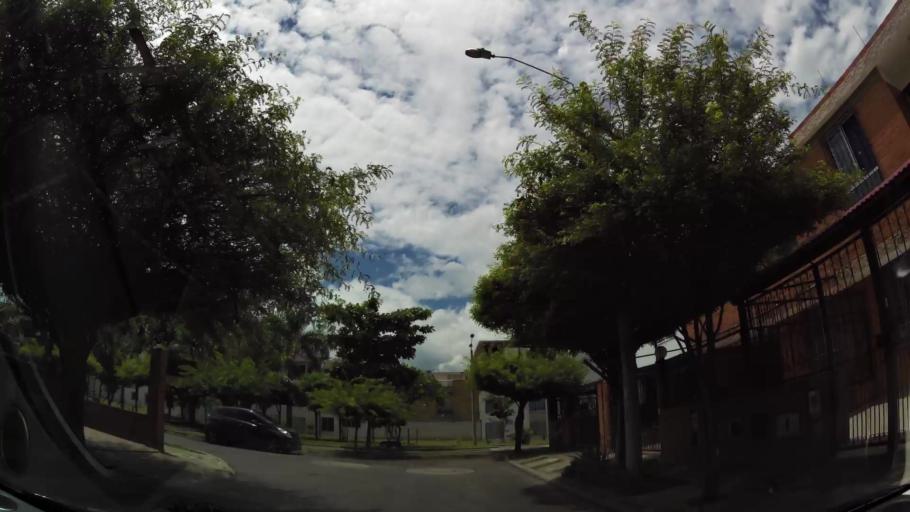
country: CO
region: Valle del Cauca
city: Cali
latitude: 3.3773
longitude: -76.5150
